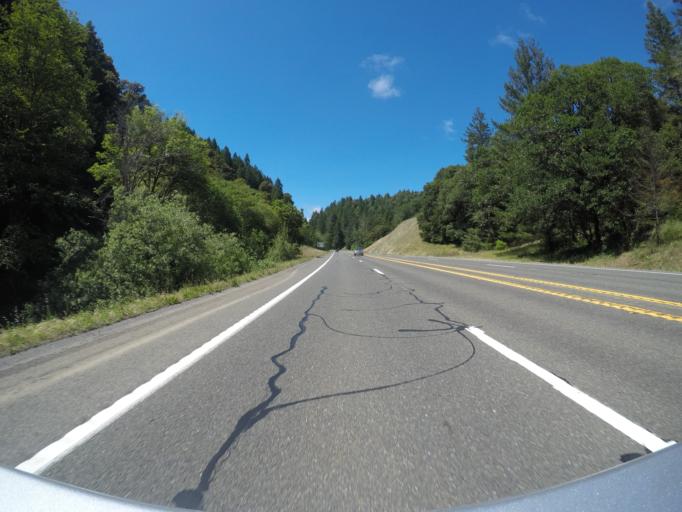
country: US
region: California
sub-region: Mendocino County
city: Laytonville
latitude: 39.5676
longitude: -123.4353
